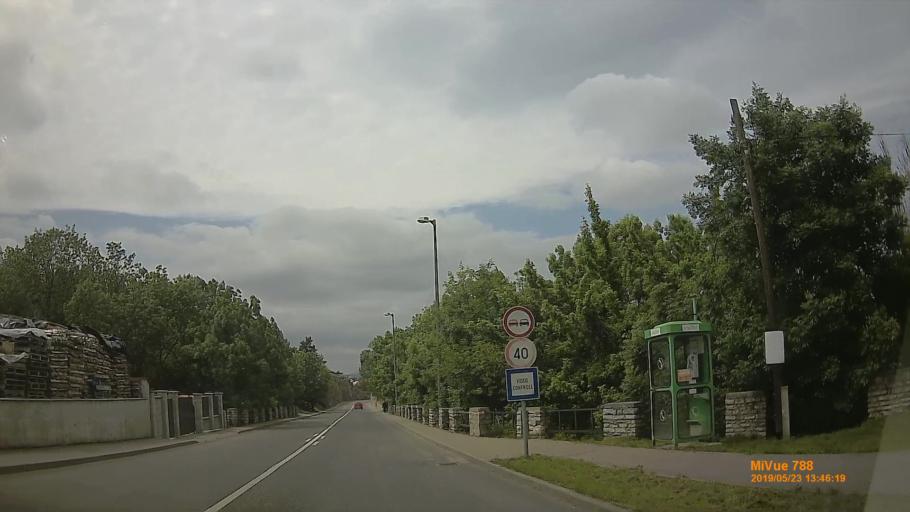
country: HU
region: Veszprem
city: Veszprem
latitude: 47.0949
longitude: 17.8991
